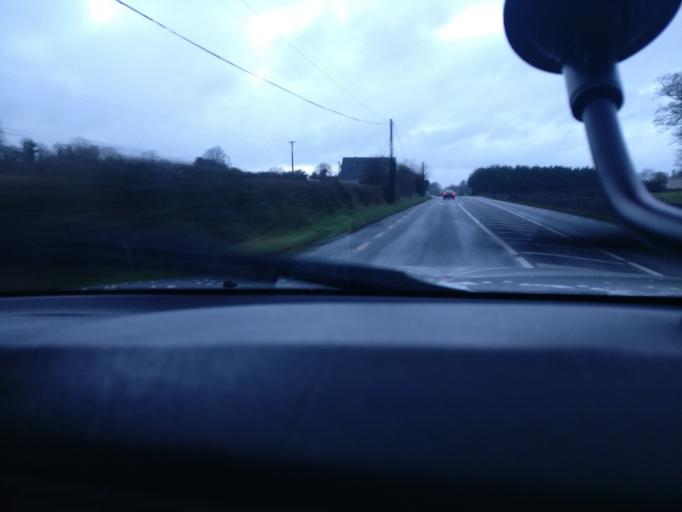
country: IE
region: Connaught
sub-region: County Galway
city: Ballinasloe
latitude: 53.3118
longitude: -8.2762
